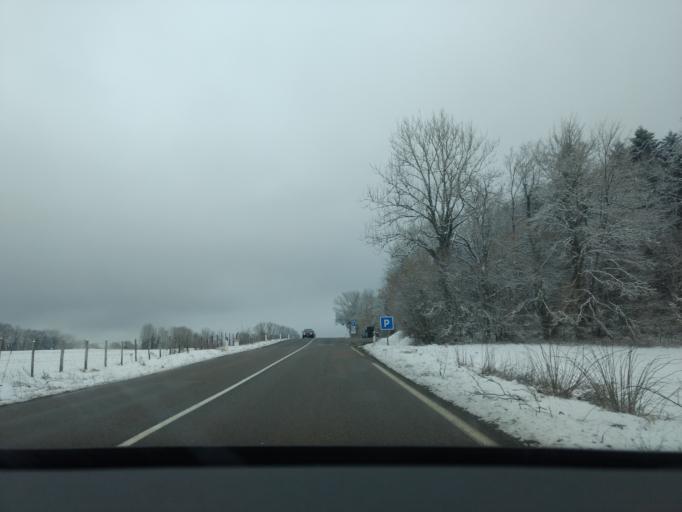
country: FR
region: Franche-Comte
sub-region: Departement du Jura
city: Champagnole
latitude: 46.7906
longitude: 5.8449
